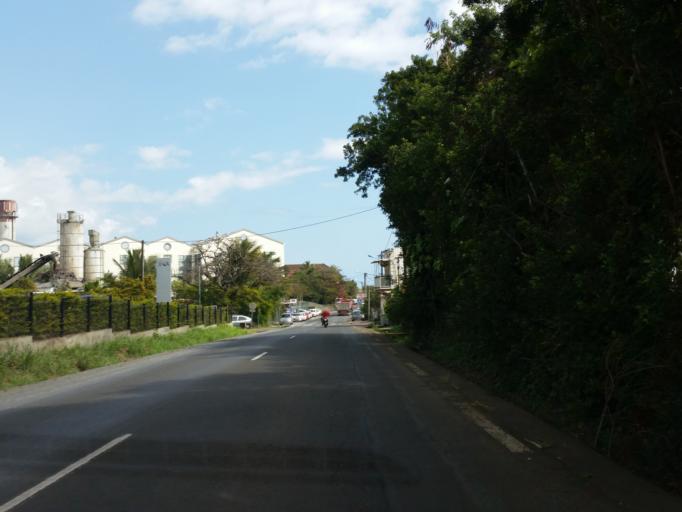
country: RE
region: Reunion
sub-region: Reunion
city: Sainte-Marie
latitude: -20.8944
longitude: 55.5355
